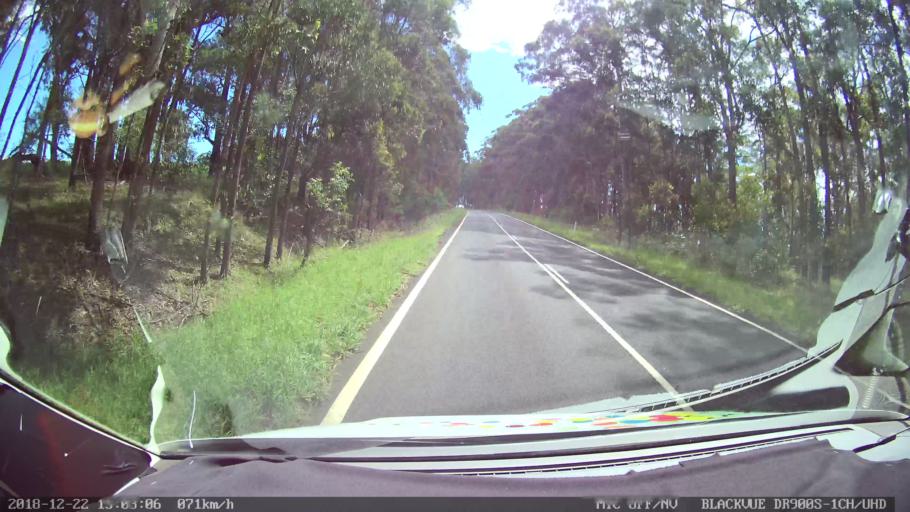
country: AU
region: New South Wales
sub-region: Bellingen
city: Dorrigo
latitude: -30.2620
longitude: 152.4435
